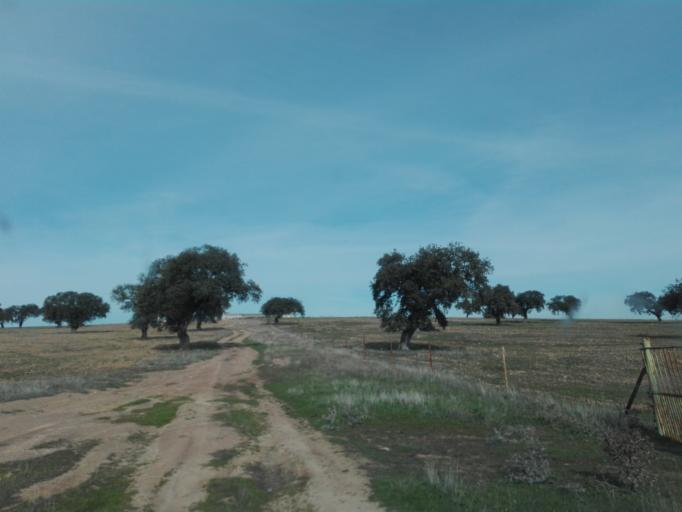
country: ES
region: Extremadura
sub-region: Provincia de Badajoz
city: Campillo de Llerena
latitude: 38.4704
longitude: -5.8899
